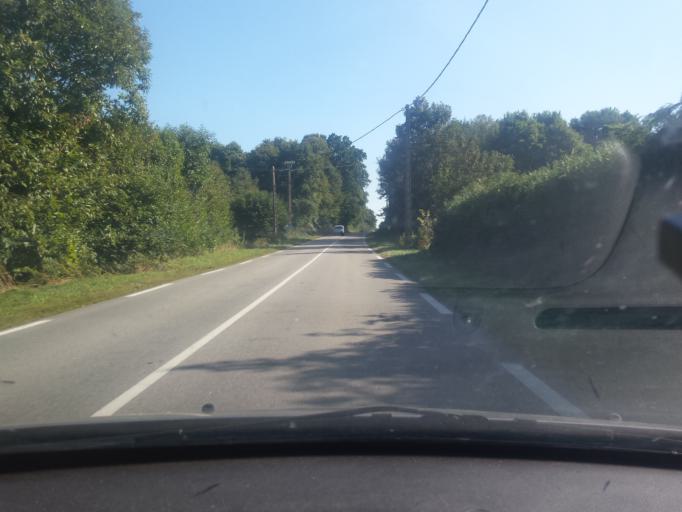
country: FR
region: Brittany
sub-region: Departement du Morbihan
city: Saint-Thuriau
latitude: 48.0380
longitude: -2.9228
